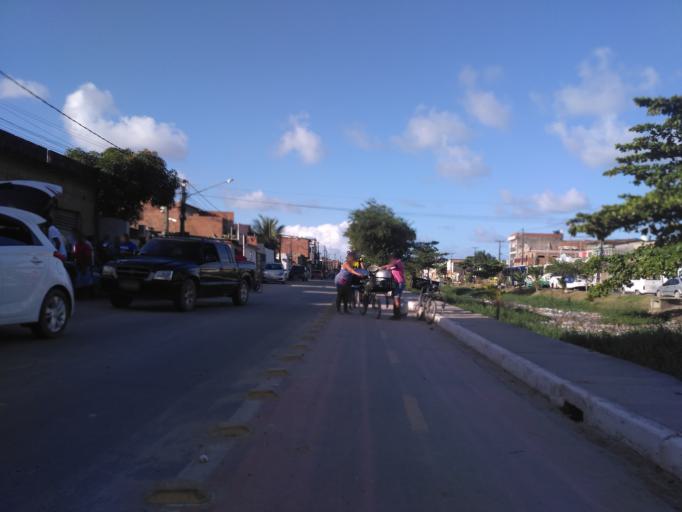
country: BR
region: Pernambuco
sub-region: Jaboatao Dos Guararapes
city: Jaboatao
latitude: -8.1846
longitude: -34.9387
